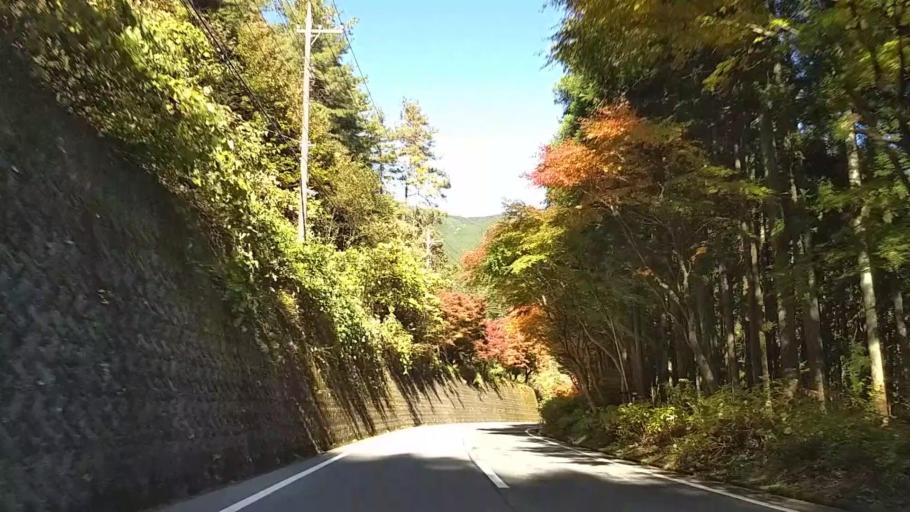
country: JP
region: Yamanashi
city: Otsuki
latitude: 35.7497
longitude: 138.9543
